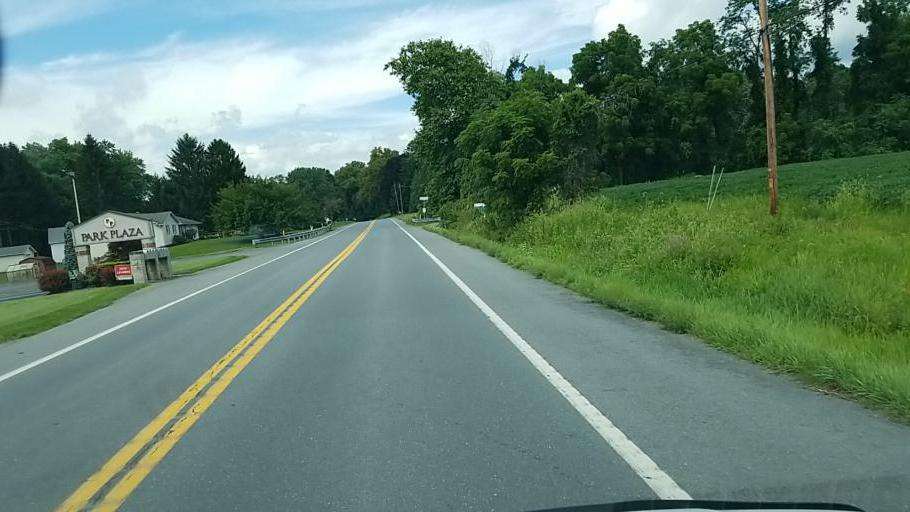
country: US
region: Pennsylvania
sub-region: Dauphin County
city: Matamoras
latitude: 40.4911
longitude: -76.9350
